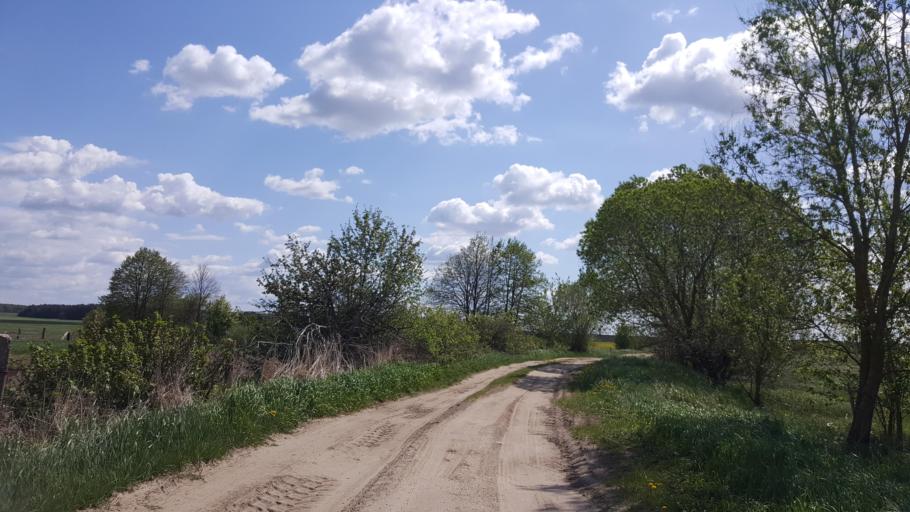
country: BY
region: Brest
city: Kamyanyets
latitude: 52.3885
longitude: 23.8884
